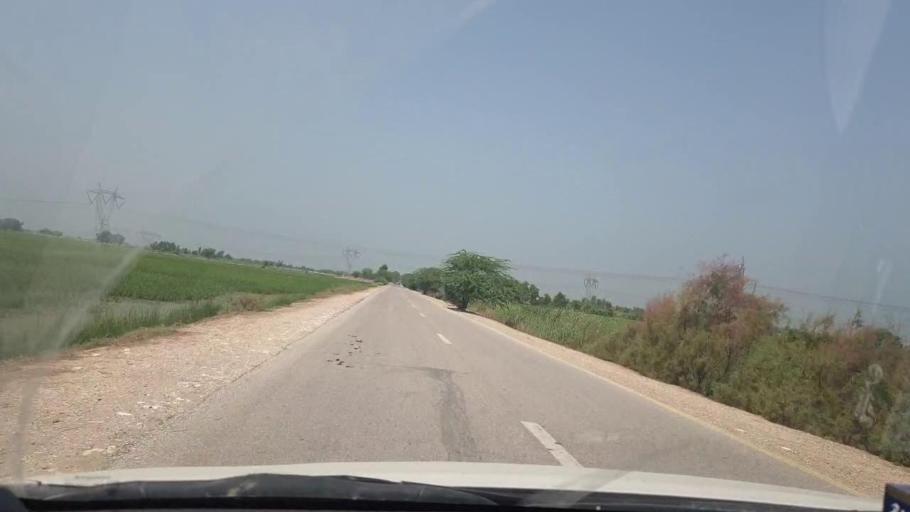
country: PK
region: Sindh
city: Rustam jo Goth
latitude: 27.9565
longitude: 68.7374
